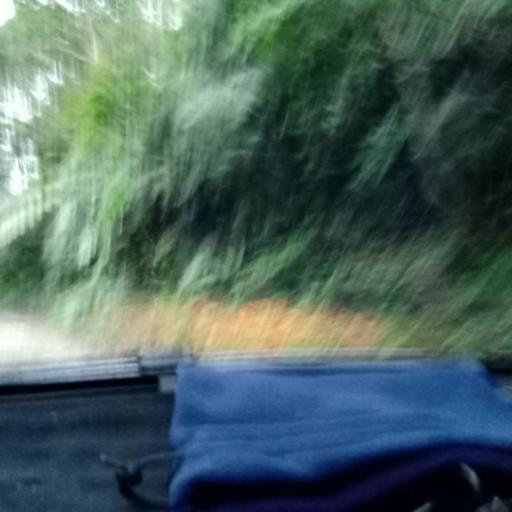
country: TW
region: Taiwan
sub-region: Yilan
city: Yilan
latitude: 24.8090
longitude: 121.6934
